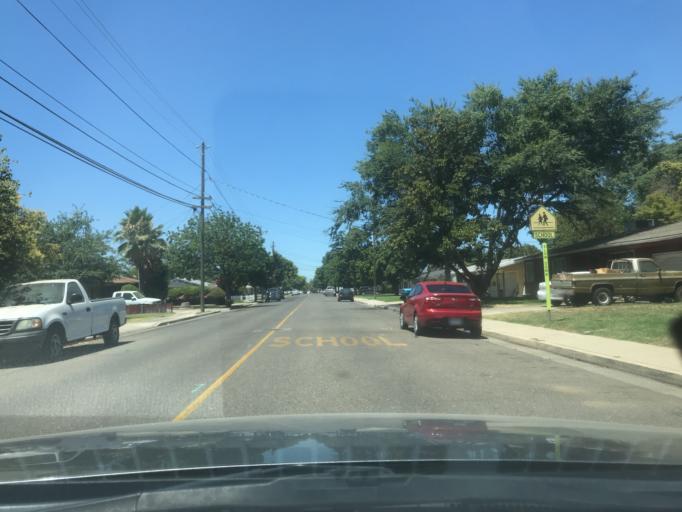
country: US
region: California
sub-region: Merced County
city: Atwater
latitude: 37.3450
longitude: -120.5969
